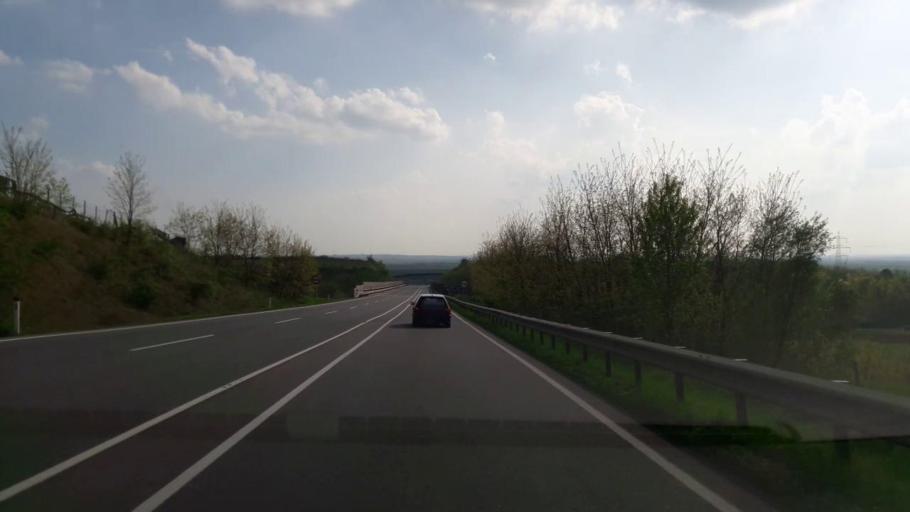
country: AT
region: Lower Austria
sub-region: Politischer Bezirk Hollabrunn
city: Haugsdorf
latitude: 48.7324
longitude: 16.0557
